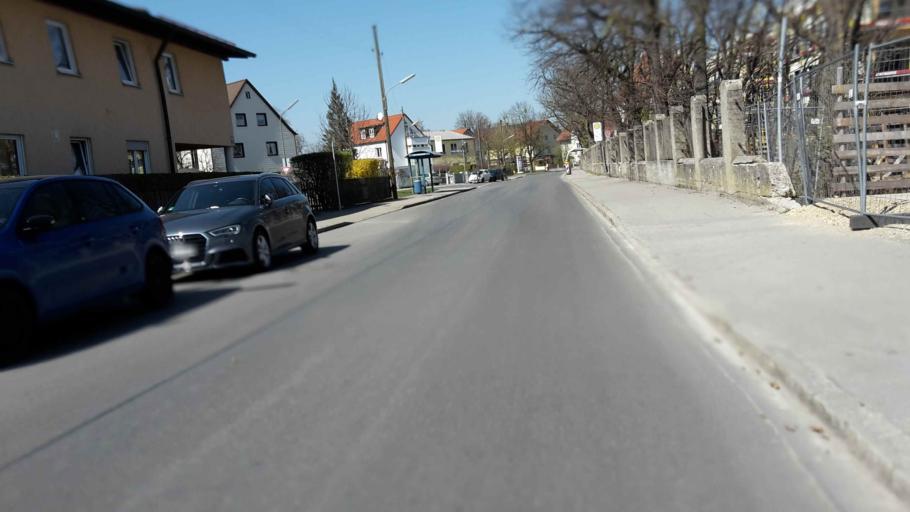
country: DE
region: Bavaria
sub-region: Upper Bavaria
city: Karlsfeld
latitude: 48.1960
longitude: 11.4617
